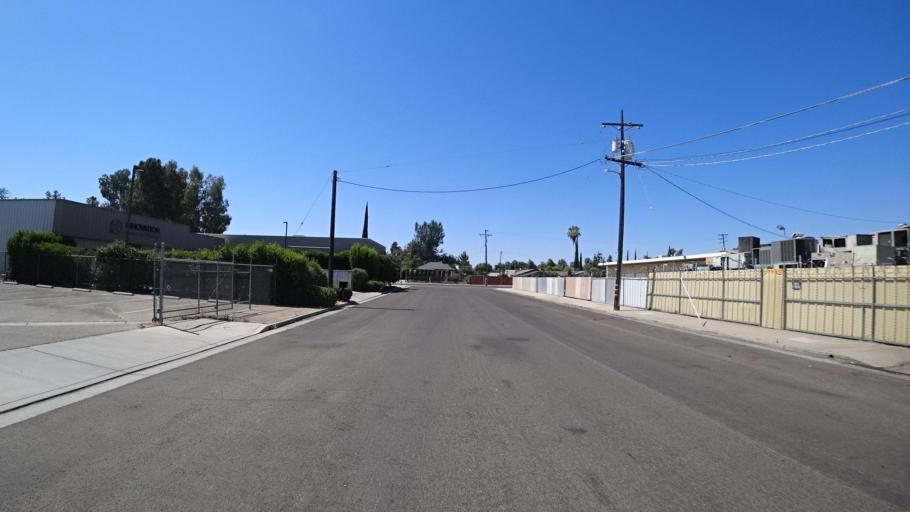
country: US
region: California
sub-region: Fresno County
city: Fresno
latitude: 36.7620
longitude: -119.7380
